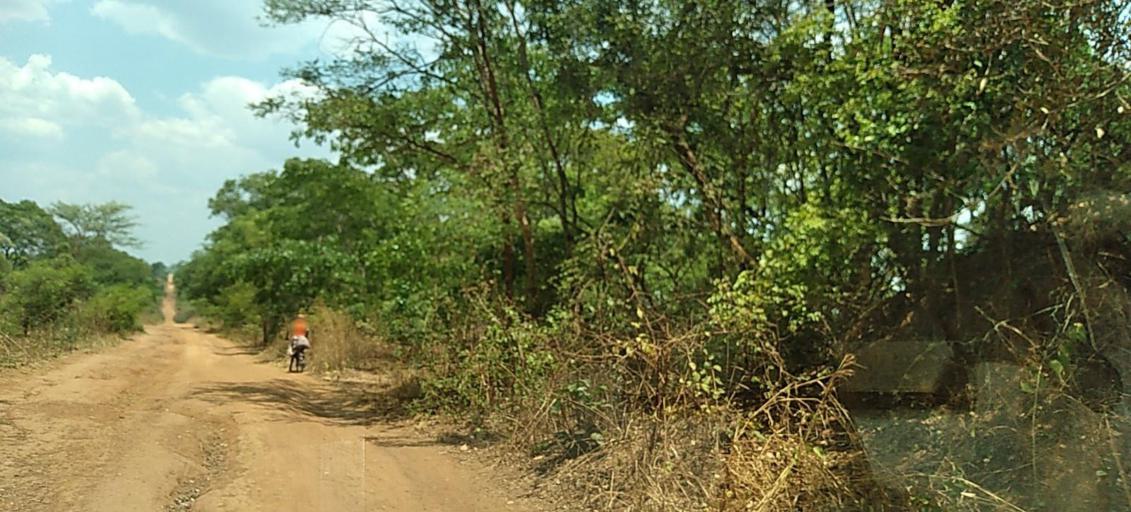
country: ZM
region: Copperbelt
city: Luanshya
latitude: -13.3885
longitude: 28.4467
